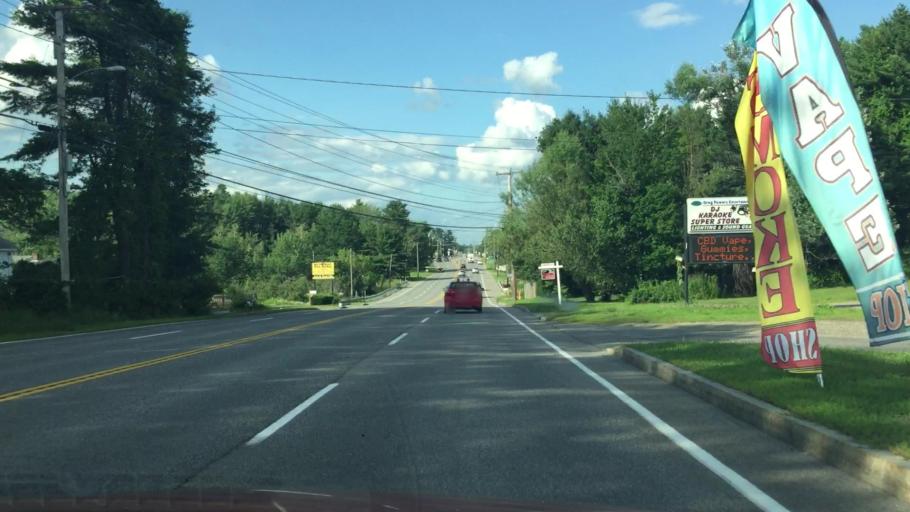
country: US
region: Maine
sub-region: Cumberland County
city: West Scarborough
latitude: 43.5429
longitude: -70.4156
